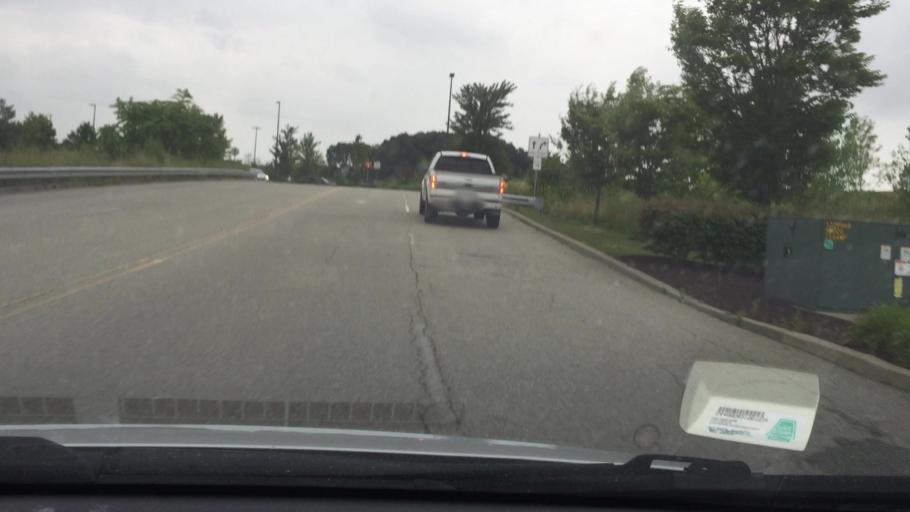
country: US
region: Pennsylvania
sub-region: Allegheny County
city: Cheswick
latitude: 40.5669
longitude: -79.8022
